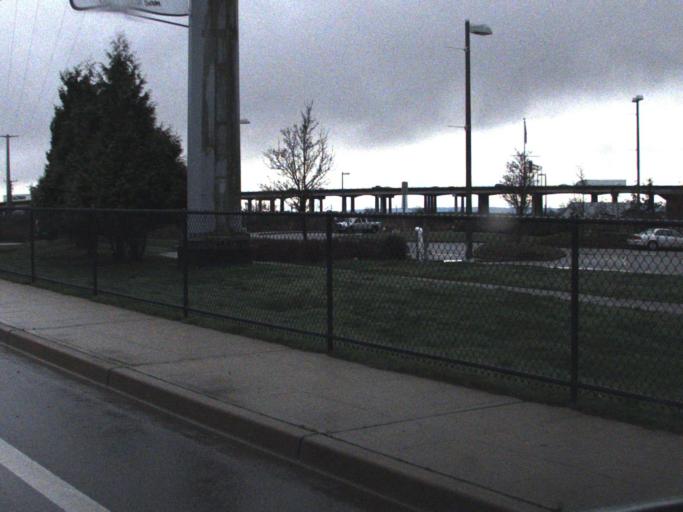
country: US
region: Washington
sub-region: Snohomish County
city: Marysville
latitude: 48.0478
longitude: -122.1773
